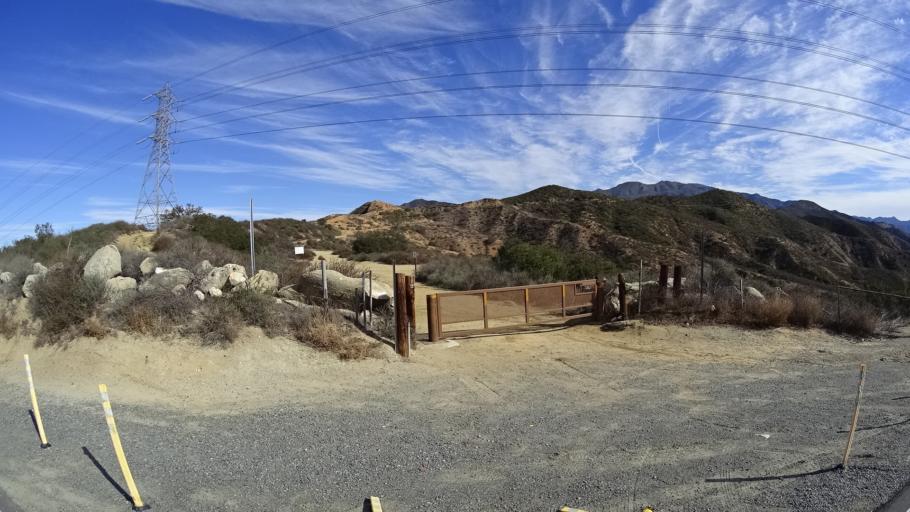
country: US
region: California
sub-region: Orange County
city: Portola Hills
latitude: 33.7023
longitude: -117.6366
